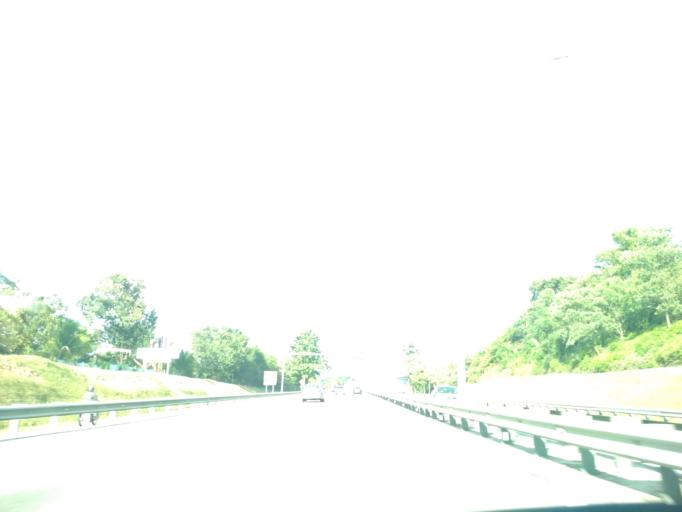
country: MY
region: Penang
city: Bukit Mertajam
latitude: 5.4051
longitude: 100.4825
